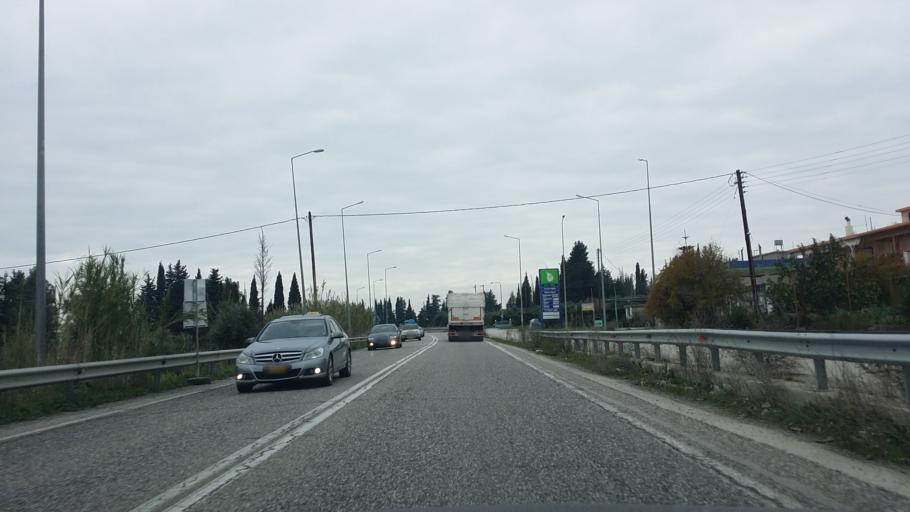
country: GR
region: West Greece
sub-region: Nomos Aitolias kai Akarnanias
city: Mesolongi
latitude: 38.3793
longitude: 21.4879
